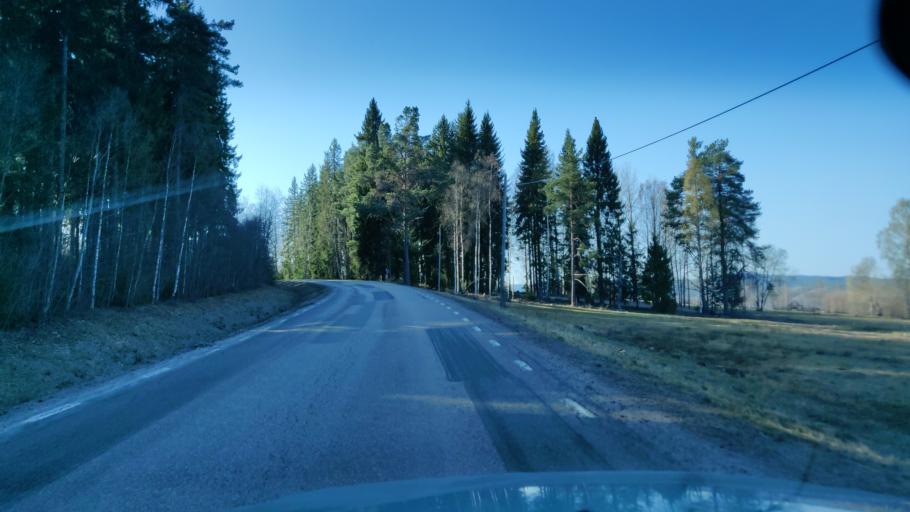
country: SE
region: Vaermland
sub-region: Munkfors Kommun
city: Munkfors
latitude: 59.9689
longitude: 13.4636
